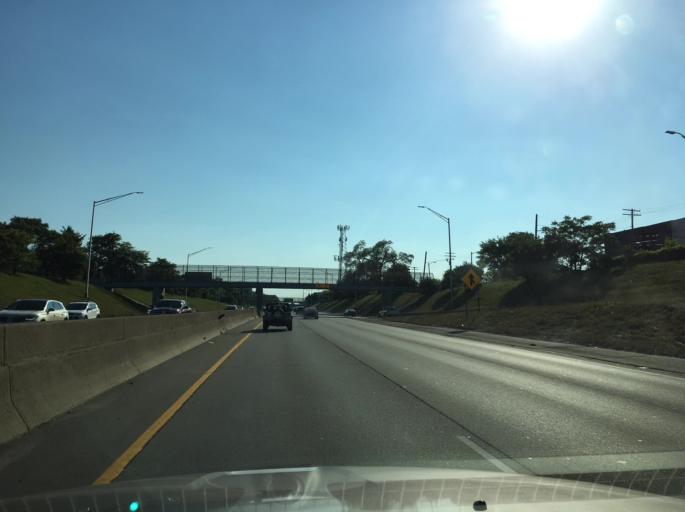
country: US
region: Michigan
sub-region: Wayne County
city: Grosse Pointe Park
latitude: 42.4035
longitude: -82.9654
